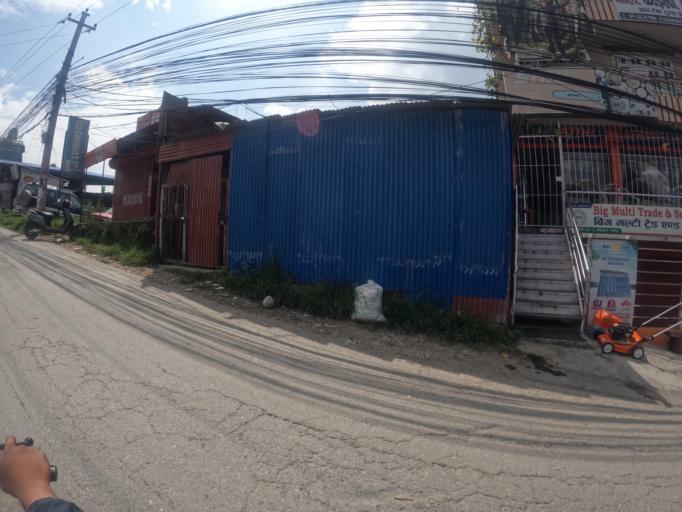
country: NP
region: Central Region
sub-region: Bagmati Zone
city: Patan
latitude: 27.6741
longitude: 85.3686
